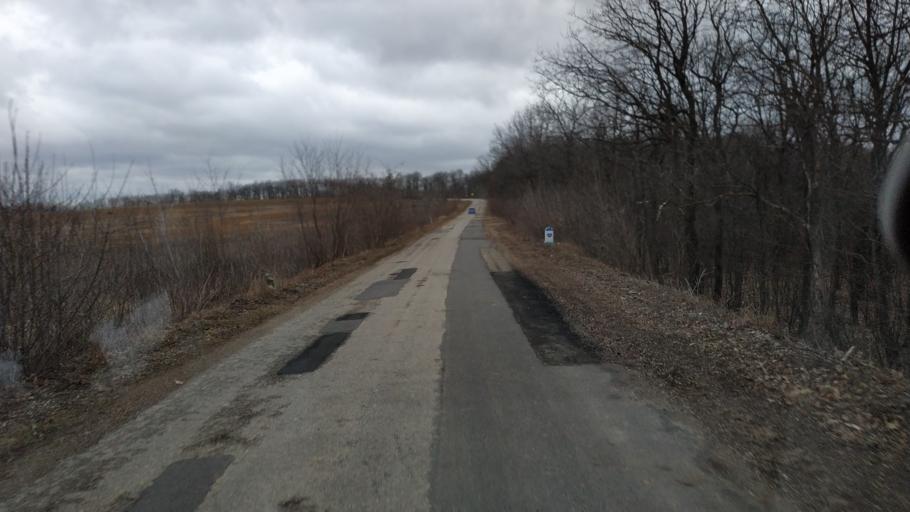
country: MD
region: Calarasi
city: Calarasi
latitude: 47.2258
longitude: 28.2388
